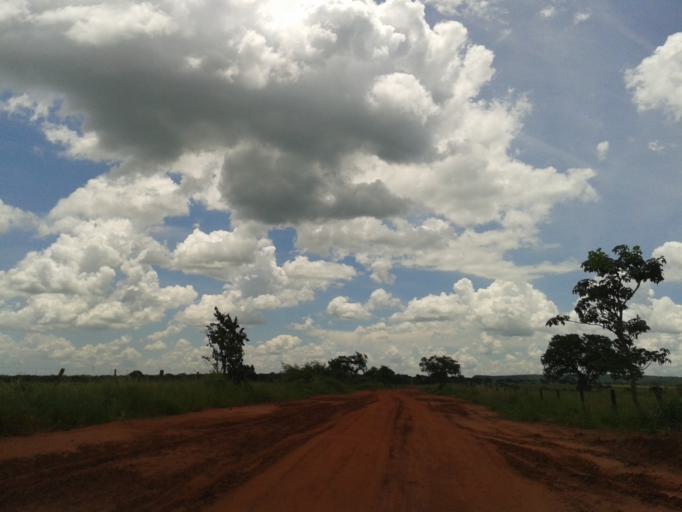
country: BR
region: Minas Gerais
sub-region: Ituiutaba
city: Ituiutaba
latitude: -18.8941
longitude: -49.4631
